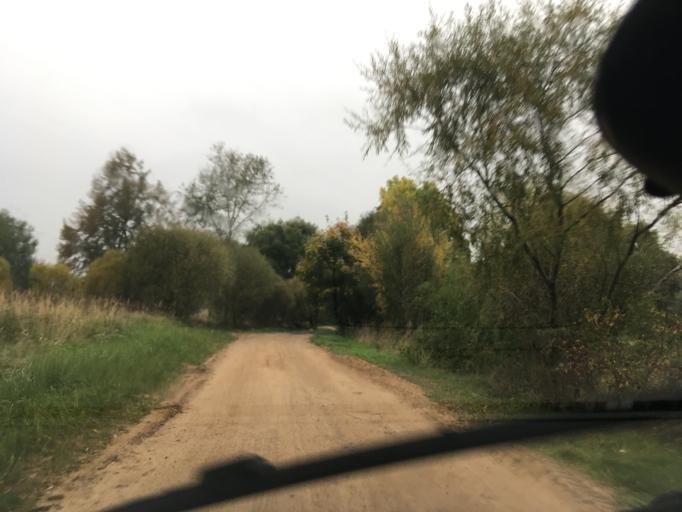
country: LV
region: Kuldigas Rajons
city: Kuldiga
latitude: 56.9844
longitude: 22.0209
